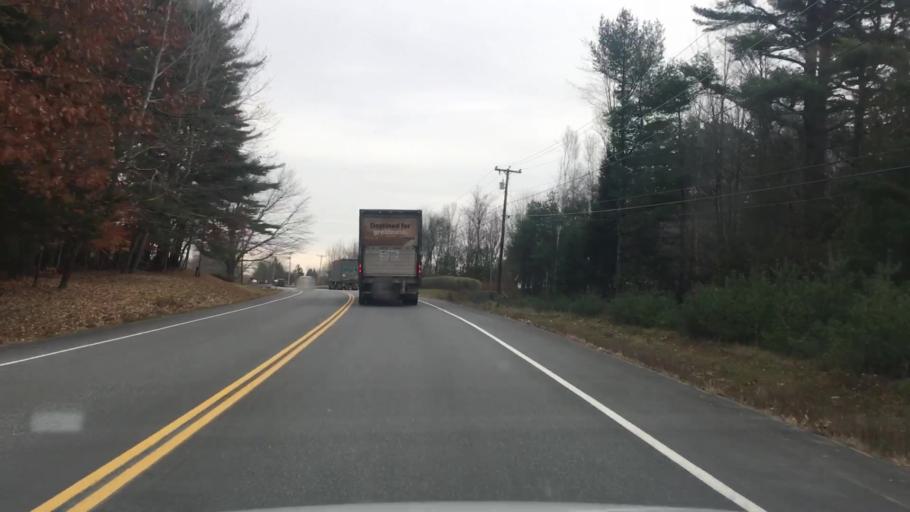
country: US
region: Maine
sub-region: Waldo County
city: Belfast
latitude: 44.4148
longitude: -69.0490
